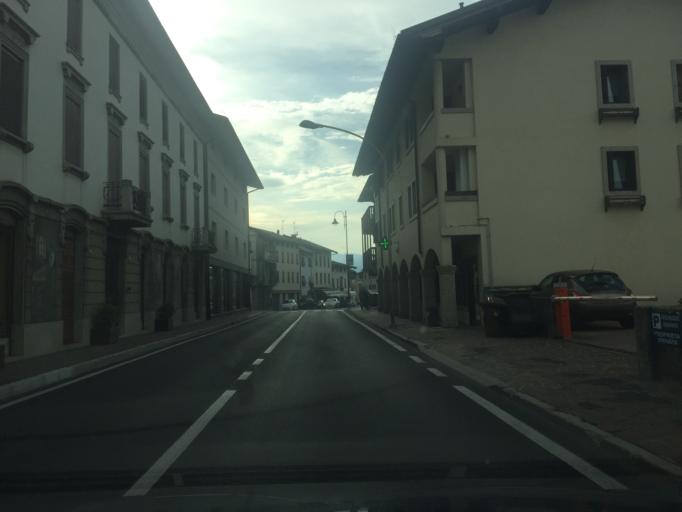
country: IT
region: Friuli Venezia Giulia
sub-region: Provincia di Udine
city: Villa Santina
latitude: 46.4164
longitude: 12.9230
